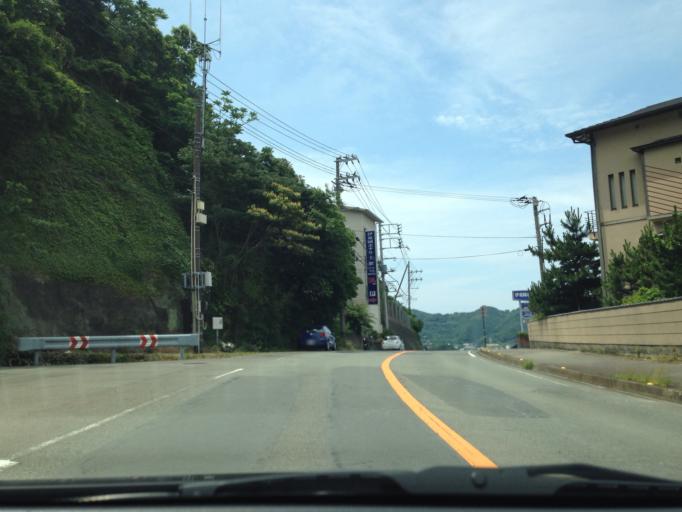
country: JP
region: Shizuoka
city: Heda
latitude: 34.9032
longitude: 138.7833
